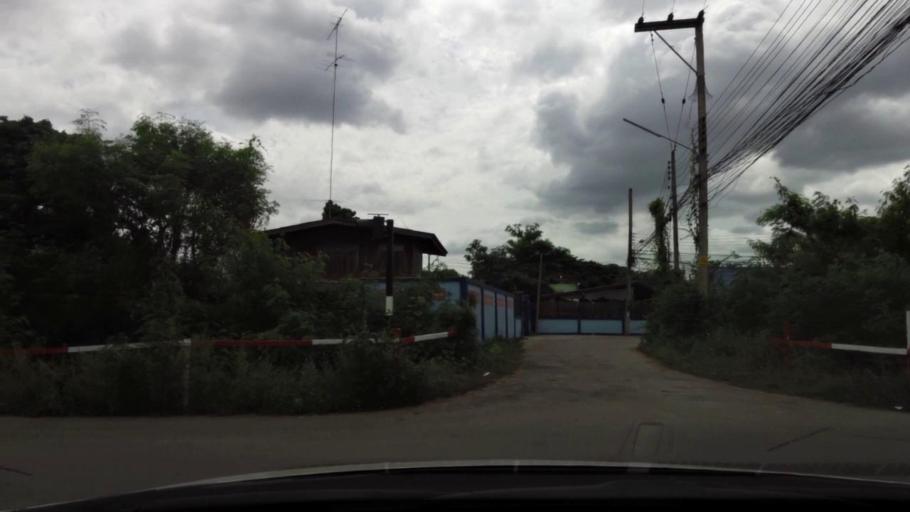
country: TH
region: Ratchaburi
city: Ratchaburi
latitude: 13.5343
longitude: 99.8331
